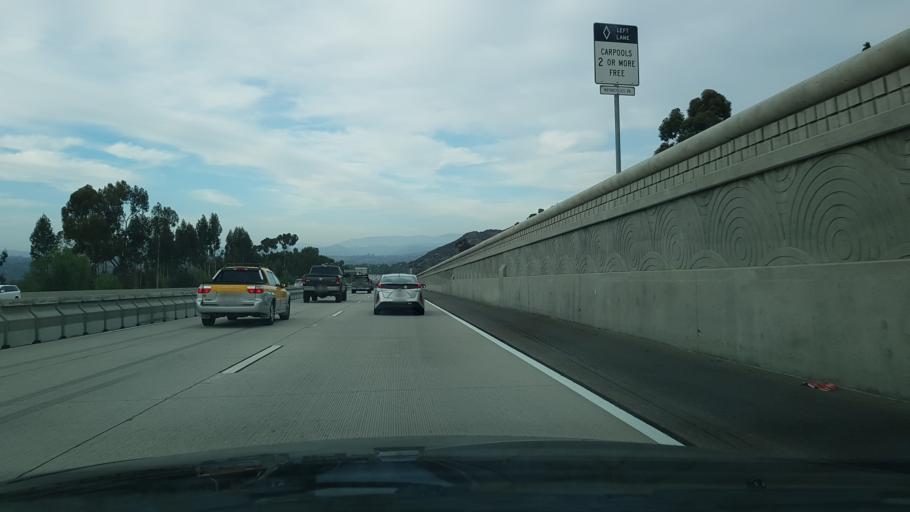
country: US
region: California
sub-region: San Diego County
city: Poway
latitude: 33.0343
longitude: -117.0773
